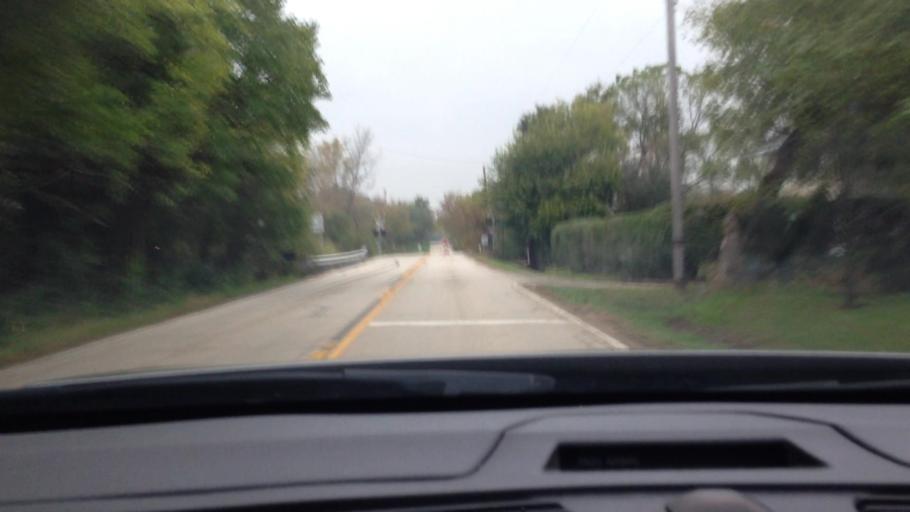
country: US
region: Illinois
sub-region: Cook County
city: Streamwood
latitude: 42.0885
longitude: -88.1946
